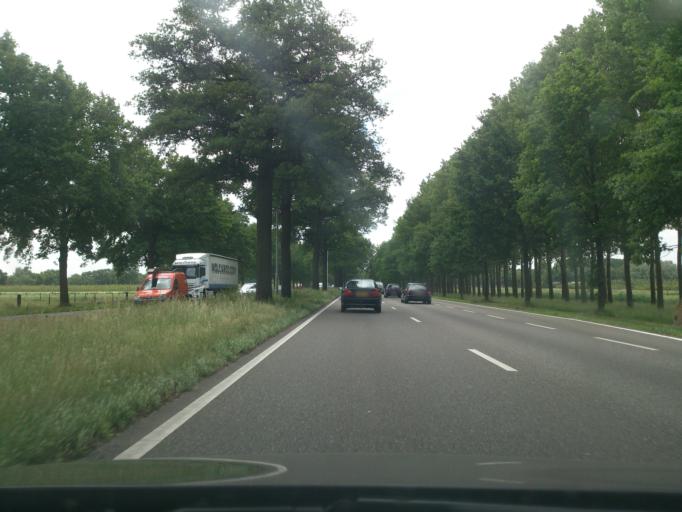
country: NL
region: North Brabant
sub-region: Gemeente Oisterwijk
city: Oisterwijk
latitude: 51.5903
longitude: 5.1668
